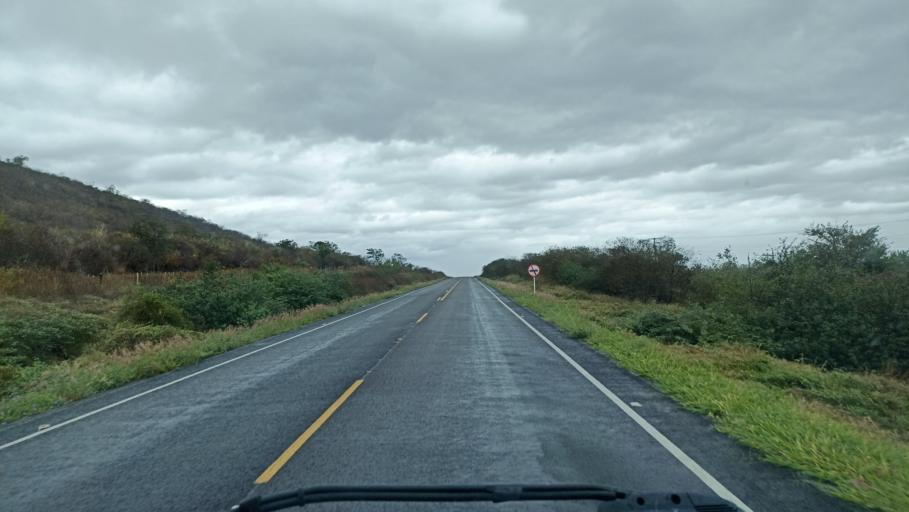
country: BR
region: Bahia
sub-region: Iacu
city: Iacu
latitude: -12.9589
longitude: -40.4740
